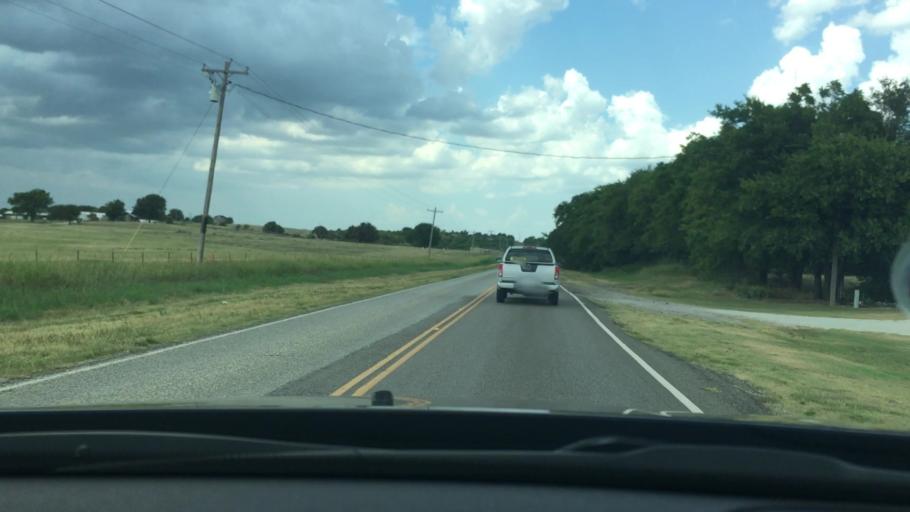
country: US
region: Oklahoma
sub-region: Pontotoc County
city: Ada
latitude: 34.5601
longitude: -96.6346
